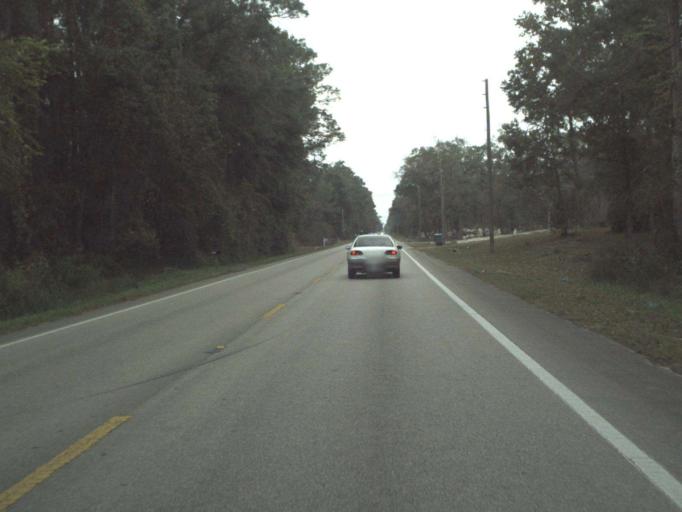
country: US
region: Florida
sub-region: Leon County
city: Woodville
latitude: 30.2544
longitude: -84.2347
